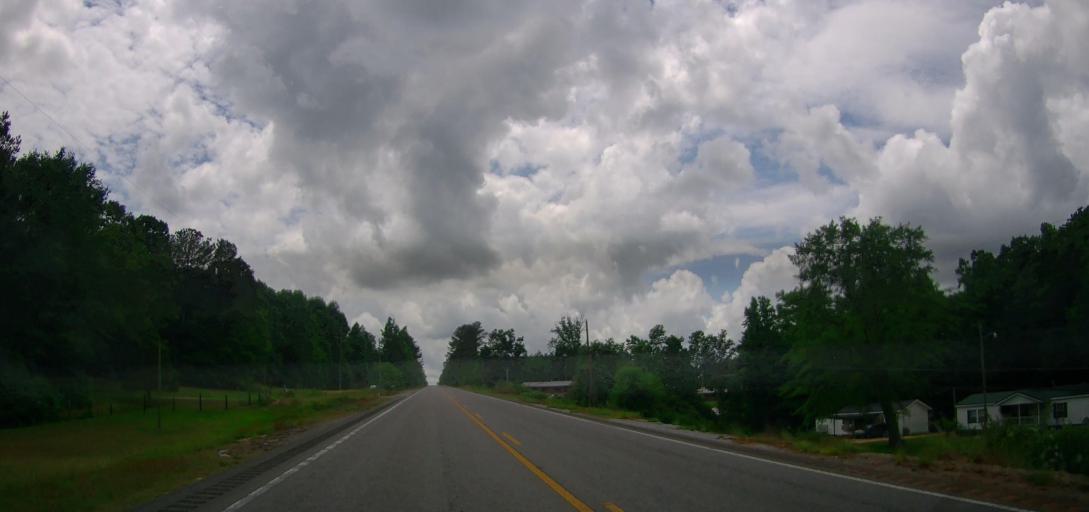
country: US
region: Alabama
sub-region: Marion County
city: Hamilton
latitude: 34.1375
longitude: -88.0026
